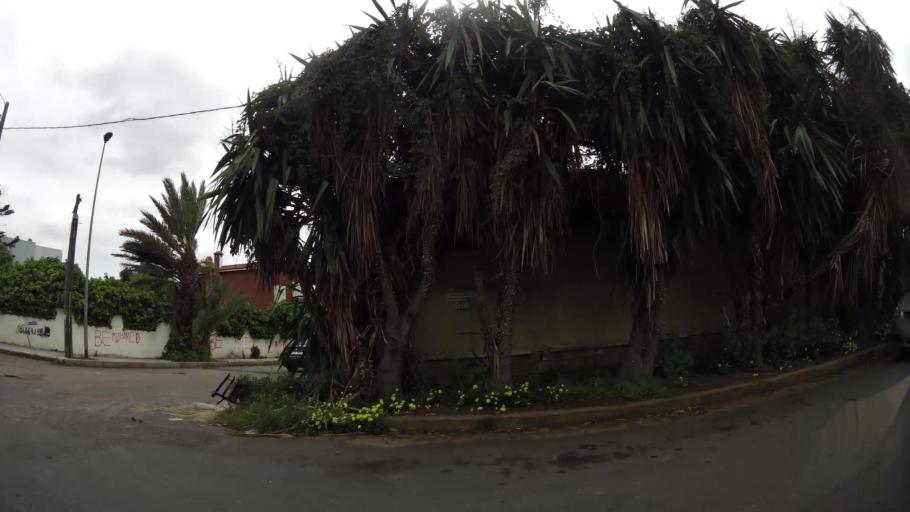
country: MA
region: Grand Casablanca
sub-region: Casablanca
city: Casablanca
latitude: 33.5534
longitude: -7.6418
